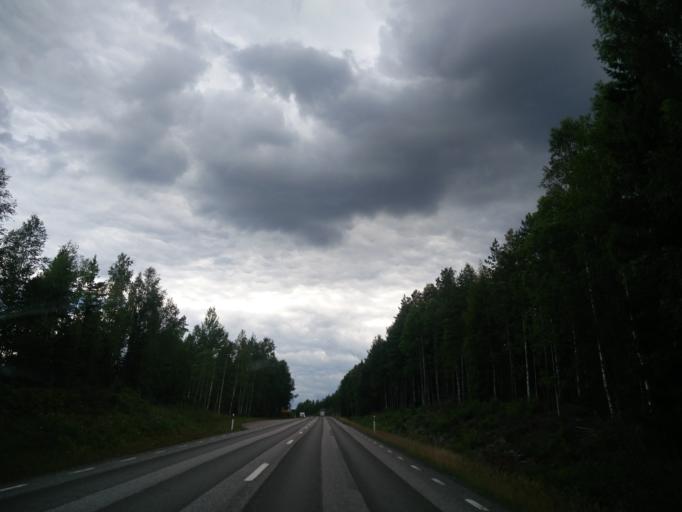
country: SE
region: OErebro
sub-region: Hallefors Kommun
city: Haellefors
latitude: 59.7856
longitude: 14.3504
